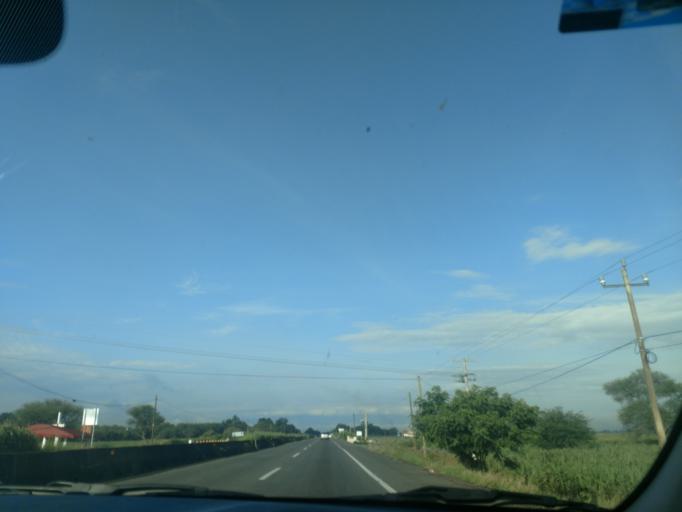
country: MX
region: Jalisco
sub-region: Ameca
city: Los Pocitos
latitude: 20.5531
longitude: -103.8932
